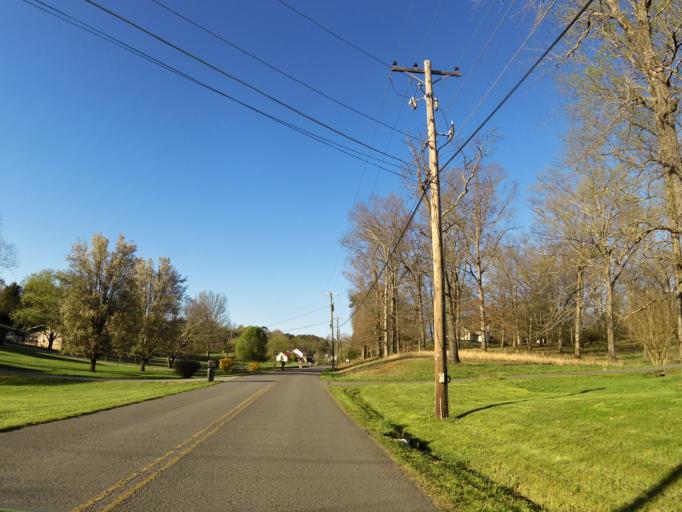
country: US
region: Tennessee
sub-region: Knox County
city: Knoxville
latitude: 35.9703
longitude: -83.8435
